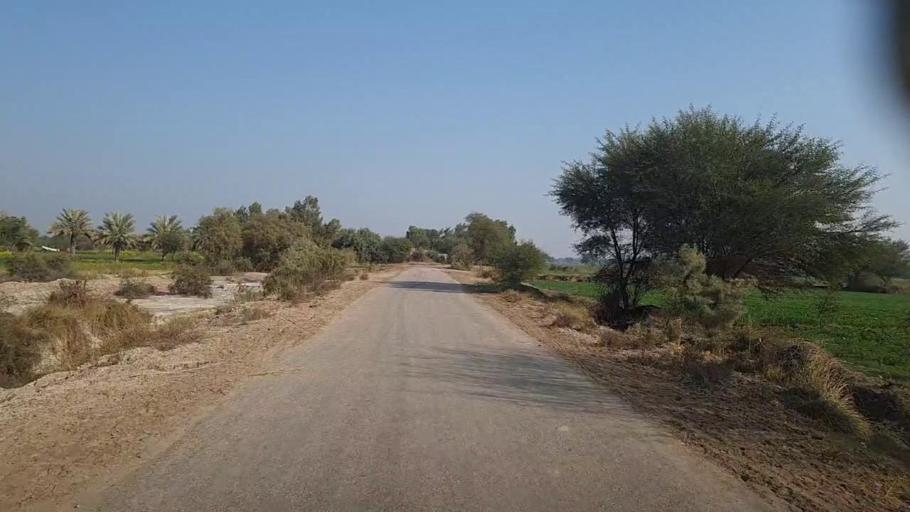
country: PK
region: Sindh
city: Mirpur Mathelo
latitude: 27.8774
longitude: 69.6083
